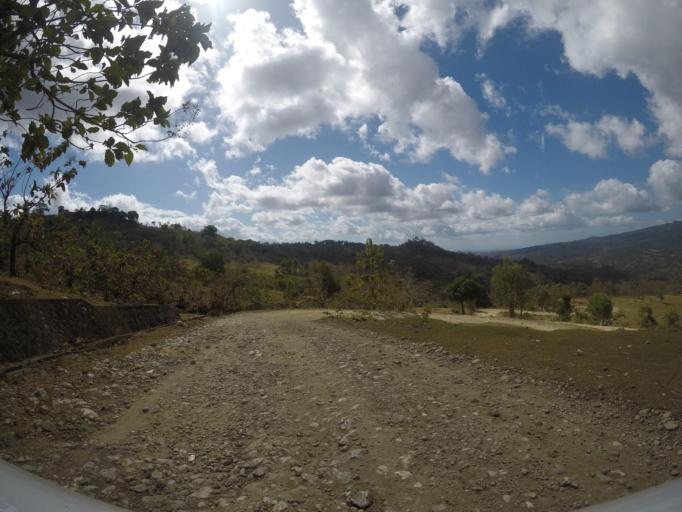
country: TL
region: Lautem
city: Lospalos
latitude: -8.5379
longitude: 126.8359
